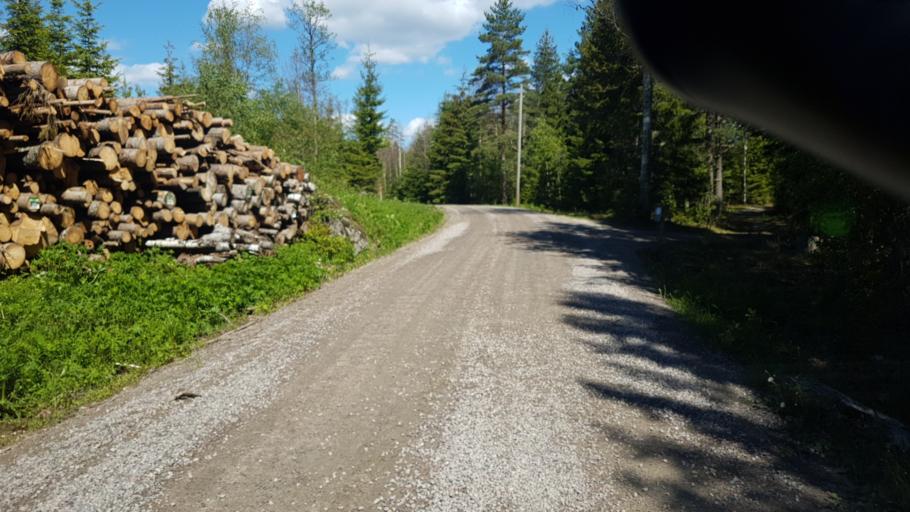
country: SE
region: Vaermland
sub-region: Arvika Kommun
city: Arvika
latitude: 59.5576
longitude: 12.8464
